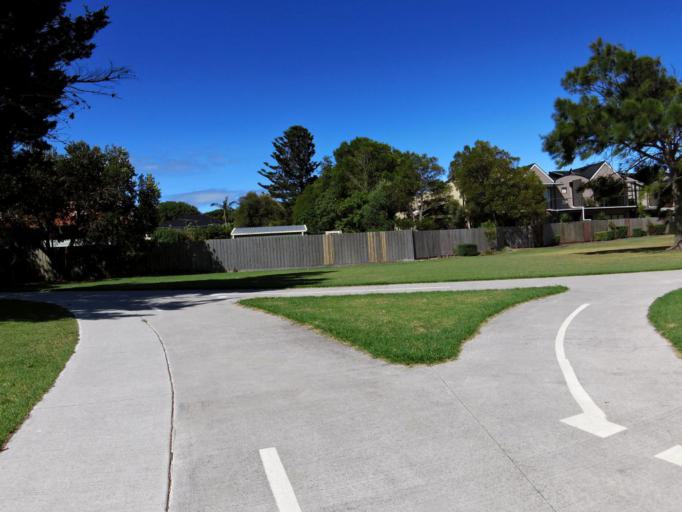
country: AU
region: Victoria
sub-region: Hobsons Bay
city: Altona
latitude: -37.8746
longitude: 144.8131
